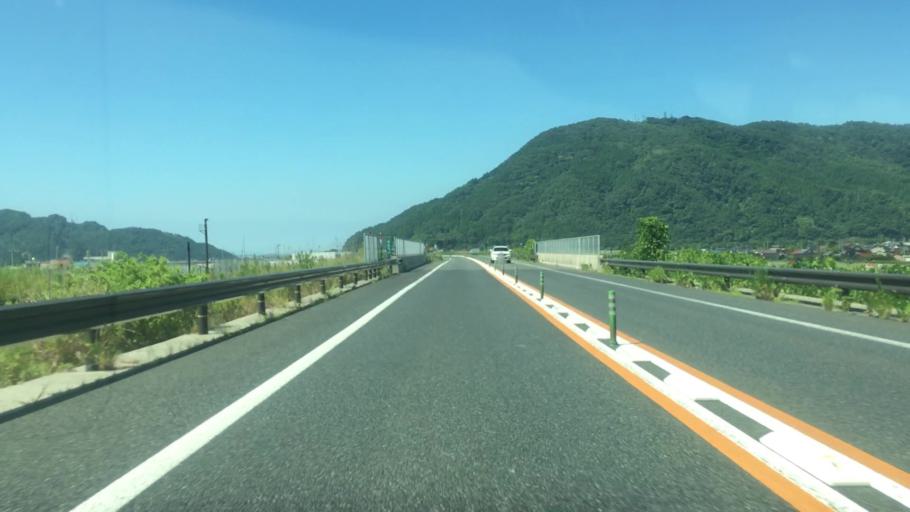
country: JP
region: Tottori
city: Tottori
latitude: 35.3939
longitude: 134.2039
